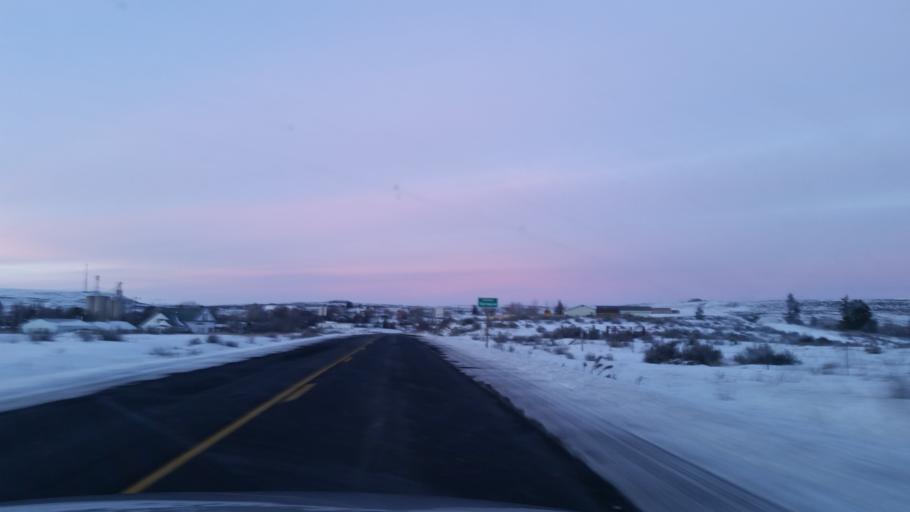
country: US
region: Washington
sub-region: Lincoln County
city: Davenport
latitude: 47.2928
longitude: -117.9722
